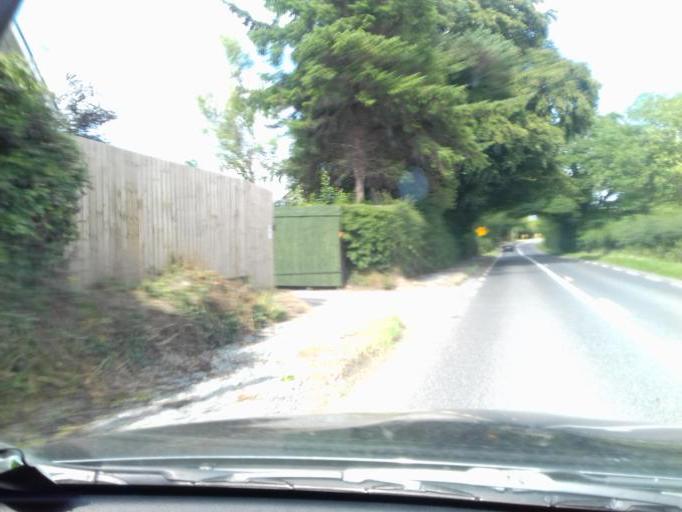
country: IE
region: Leinster
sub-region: Wicklow
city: Valleymount
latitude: 53.1141
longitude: -6.5931
